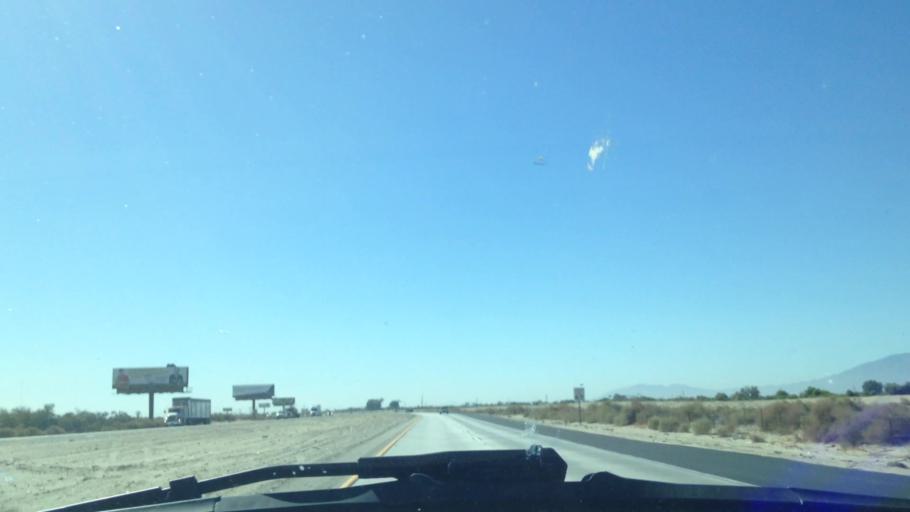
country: US
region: California
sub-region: Riverside County
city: Coachella
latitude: 33.6982
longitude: -116.1740
